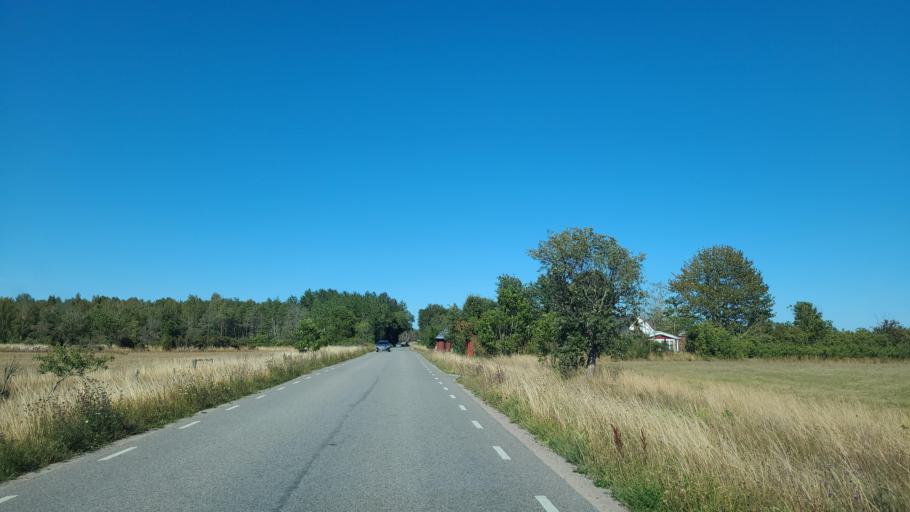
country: SE
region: Kalmar
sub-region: Borgholms Kommun
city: Borgholm
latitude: 56.9271
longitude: 16.8467
